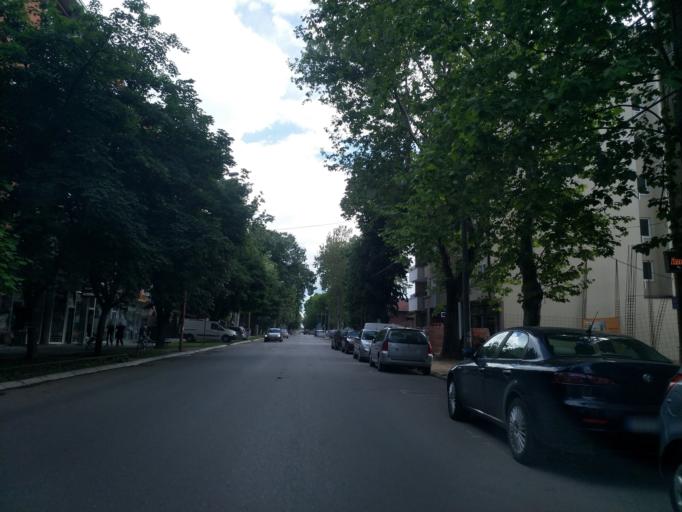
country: RS
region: Central Serbia
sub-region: Pomoravski Okrug
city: Cuprija
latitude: 43.9281
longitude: 21.3721
